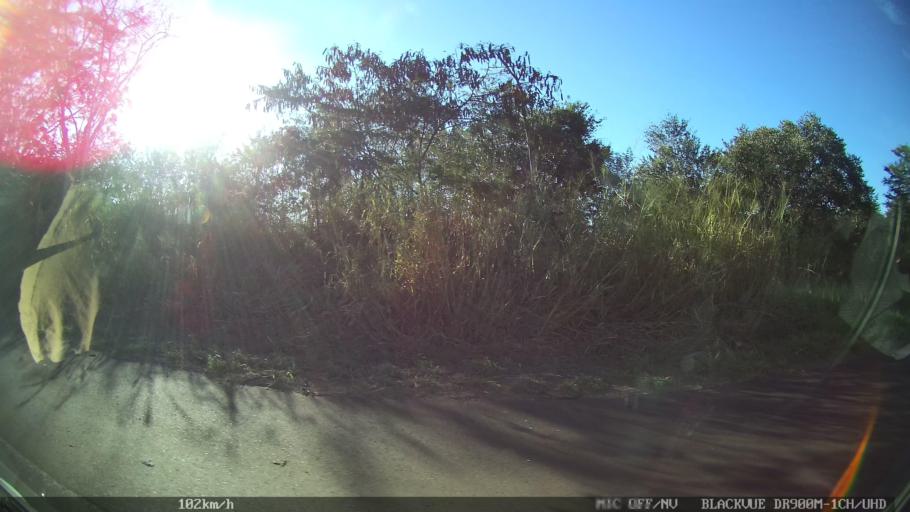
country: BR
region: Sao Paulo
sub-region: Guapiacu
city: Guapiacu
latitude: -20.7556
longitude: -49.1560
